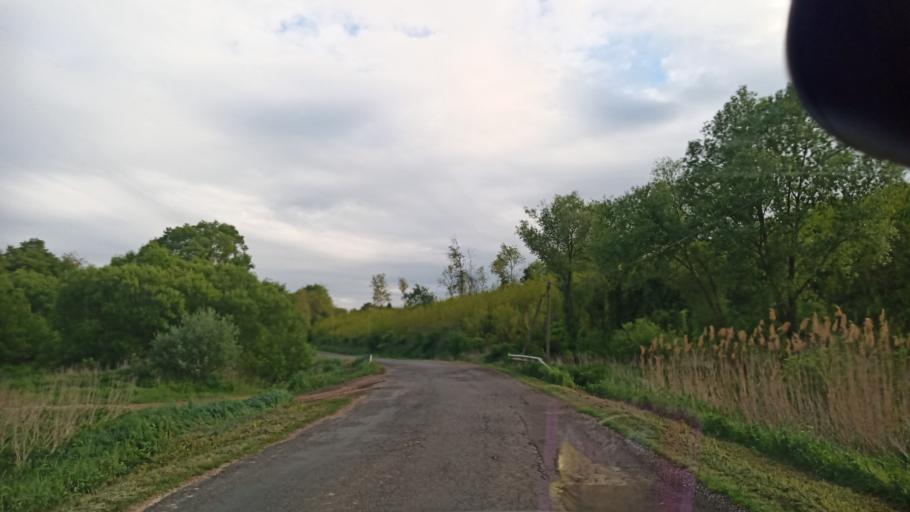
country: HU
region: Zala
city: Pacsa
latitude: 46.7318
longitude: 17.0043
